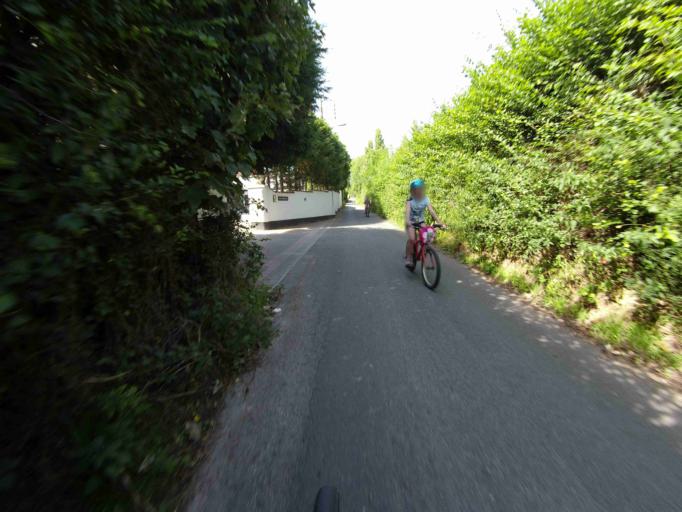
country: GB
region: England
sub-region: Devon
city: Topsham
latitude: 50.6689
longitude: -3.4410
